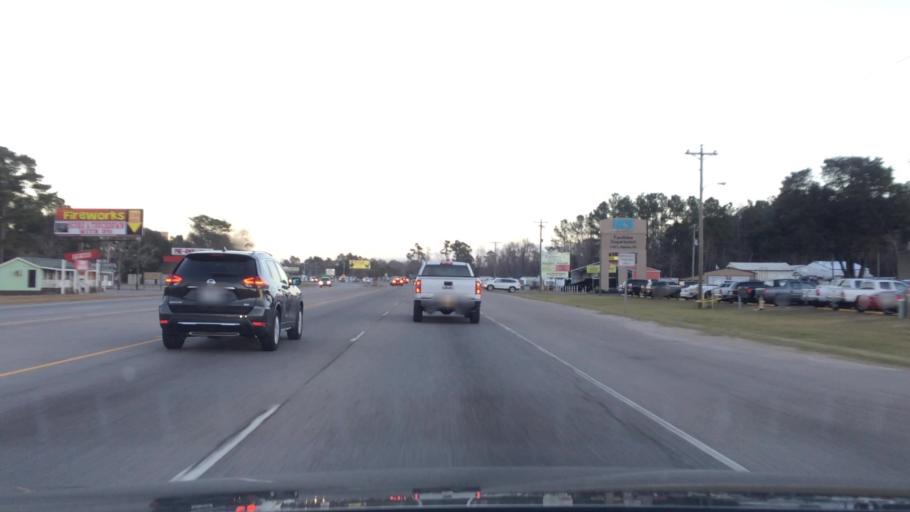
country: US
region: South Carolina
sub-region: Horry County
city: Red Hill
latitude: 33.8093
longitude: -79.0260
